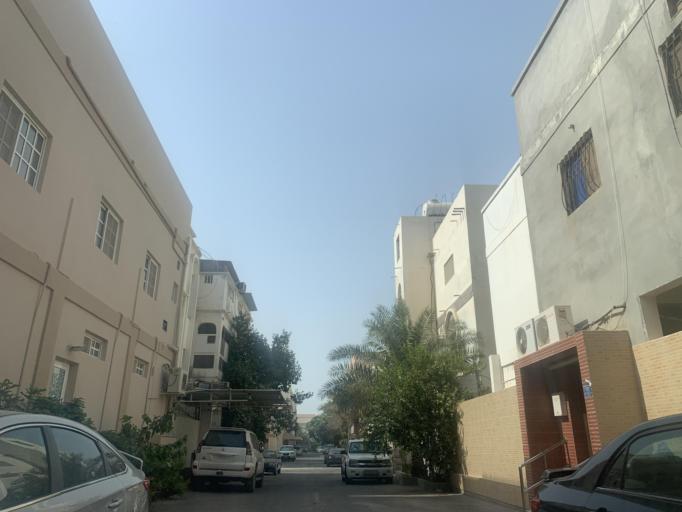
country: BH
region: Manama
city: Jidd Hafs
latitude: 26.2105
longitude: 50.4663
